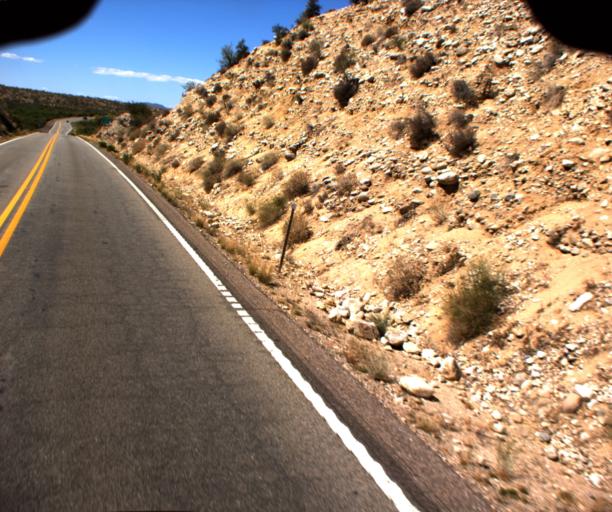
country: US
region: Arizona
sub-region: Yavapai County
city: Bagdad
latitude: 34.7958
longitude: -113.6234
